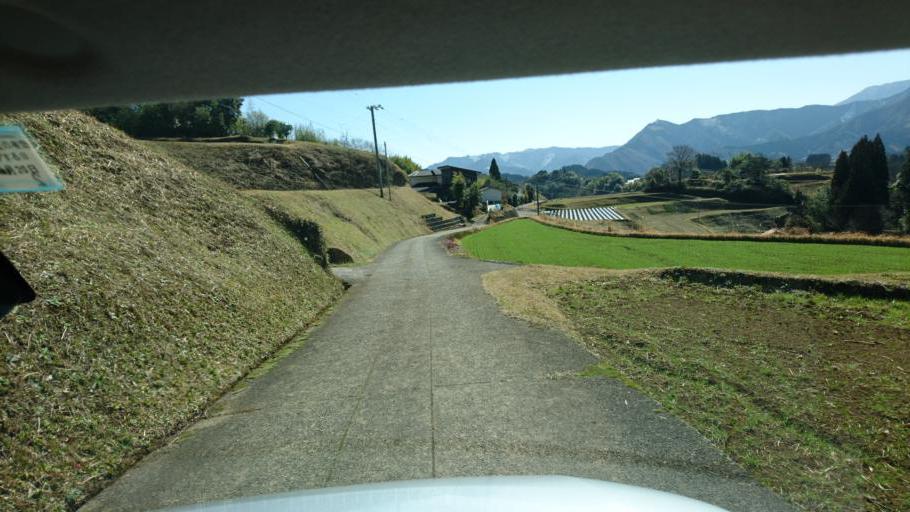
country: JP
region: Oita
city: Takedamachi
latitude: 32.7255
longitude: 131.3078
